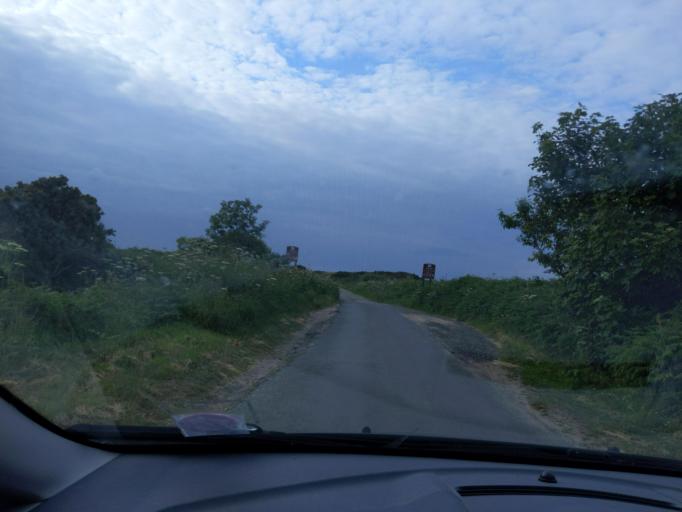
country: IM
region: Ramsey
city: Ramsey
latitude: 54.3962
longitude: -4.4444
